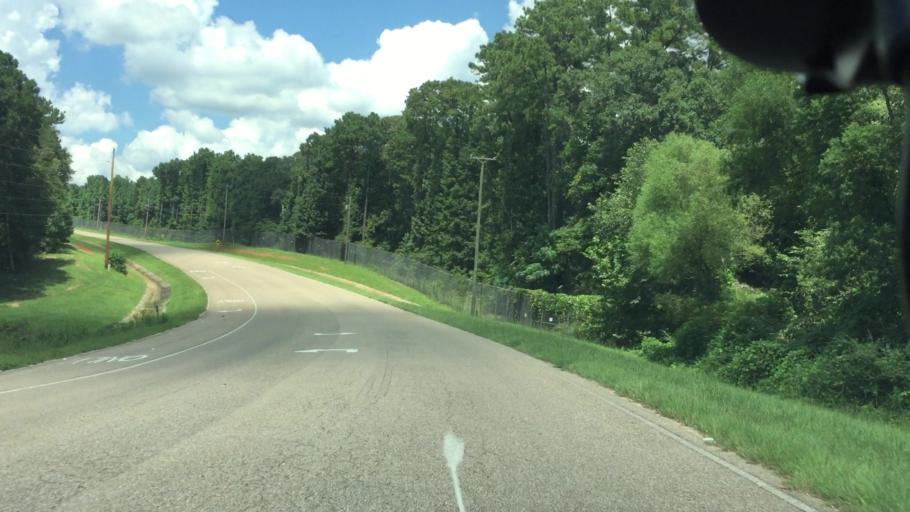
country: US
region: Alabama
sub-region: Pike County
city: Troy
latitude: 31.7754
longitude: -85.9784
